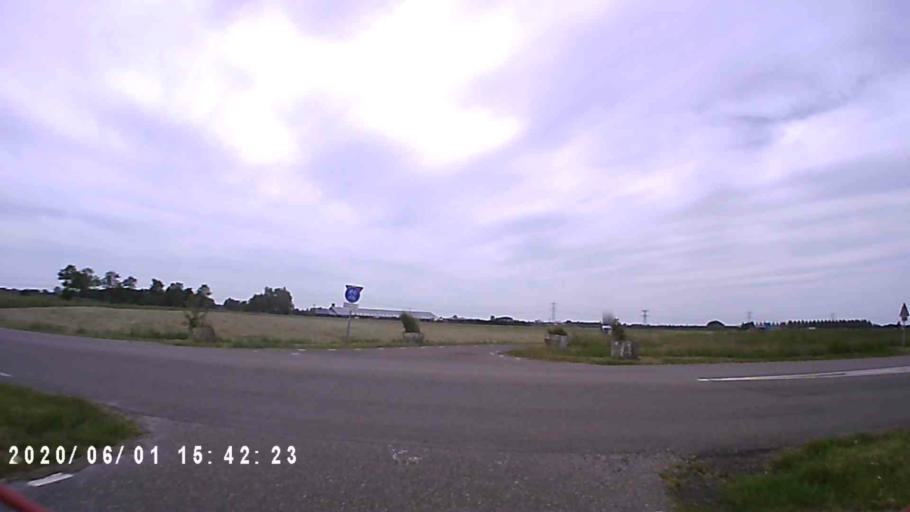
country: NL
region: Friesland
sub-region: Gemeente Boarnsterhim
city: Wergea
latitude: 53.1587
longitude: 5.8261
